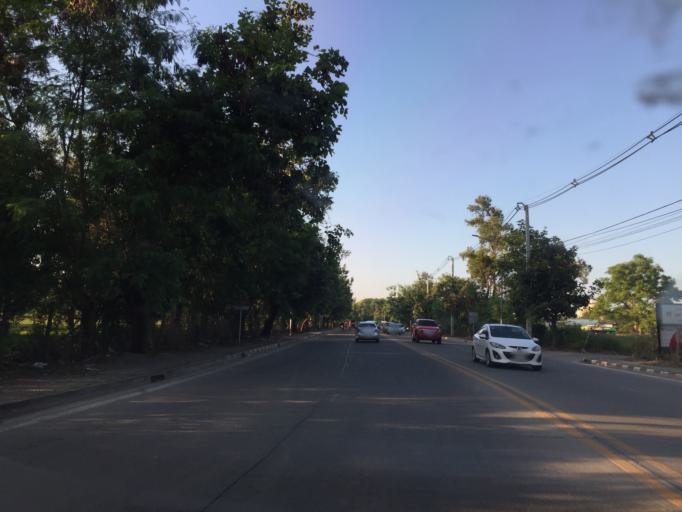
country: TH
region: Chiang Mai
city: Chiang Mai
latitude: 18.8019
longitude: 98.9954
